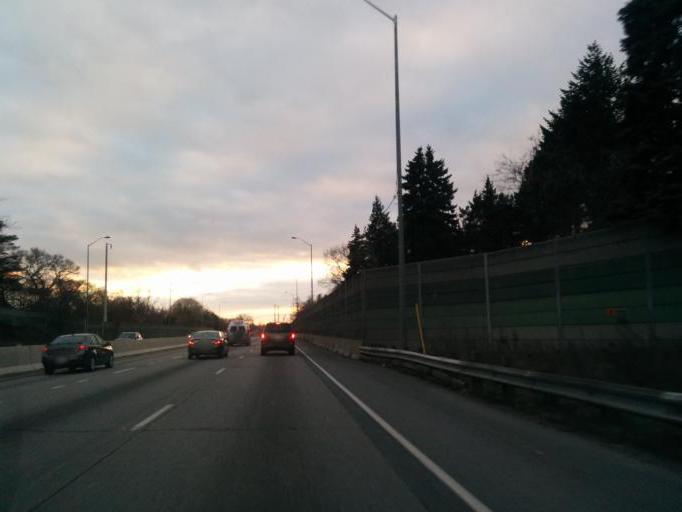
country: CA
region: Ontario
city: Mississauga
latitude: 43.5605
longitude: -79.6073
